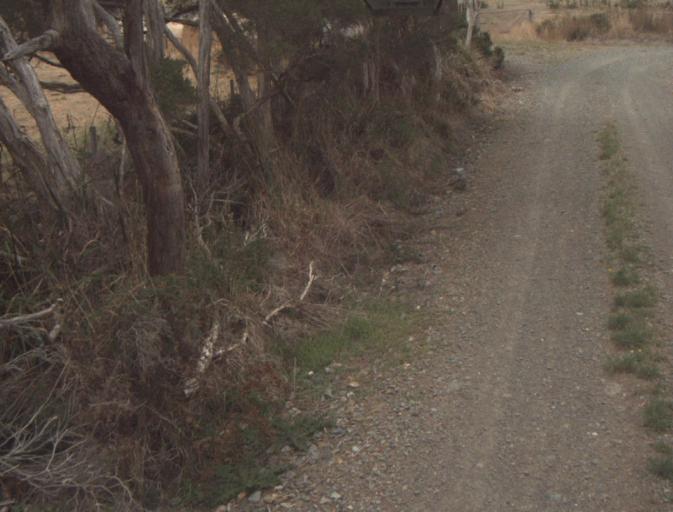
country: AU
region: Tasmania
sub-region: Launceston
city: Mayfield
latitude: -41.2426
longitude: 147.1648
